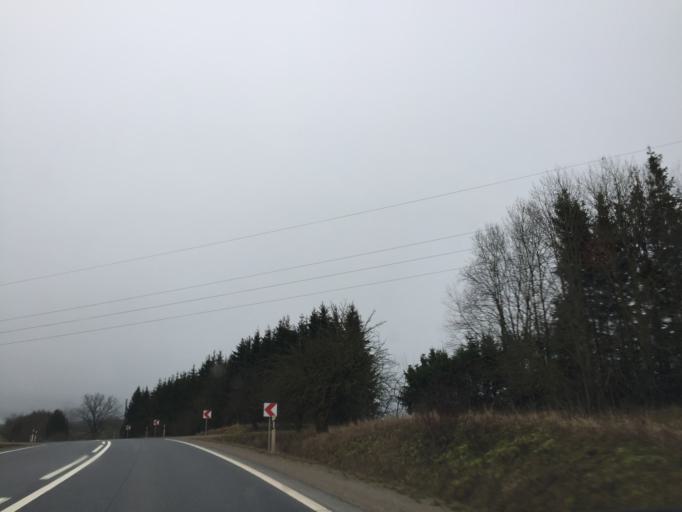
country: LV
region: Aizpute
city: Aizpute
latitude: 56.5892
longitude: 21.5883
